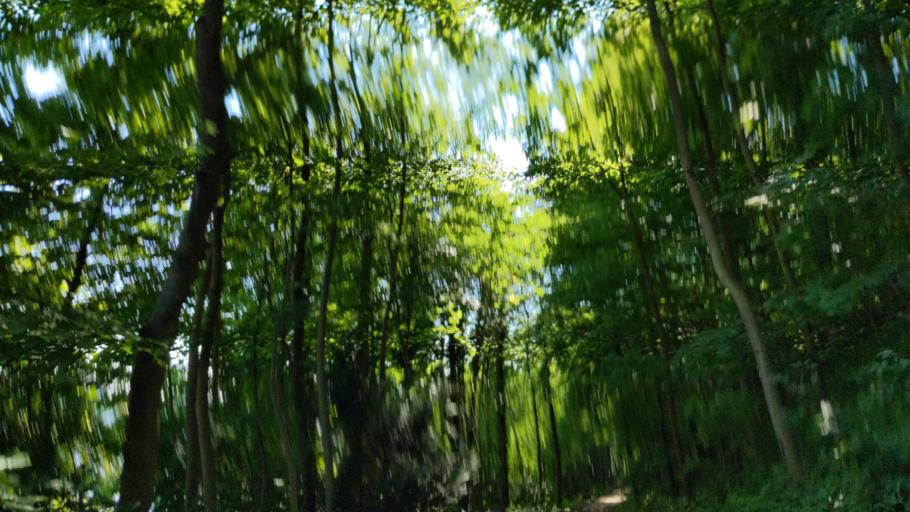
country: DE
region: Schleswig-Holstein
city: Romnitz
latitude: 53.7019
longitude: 10.7536
